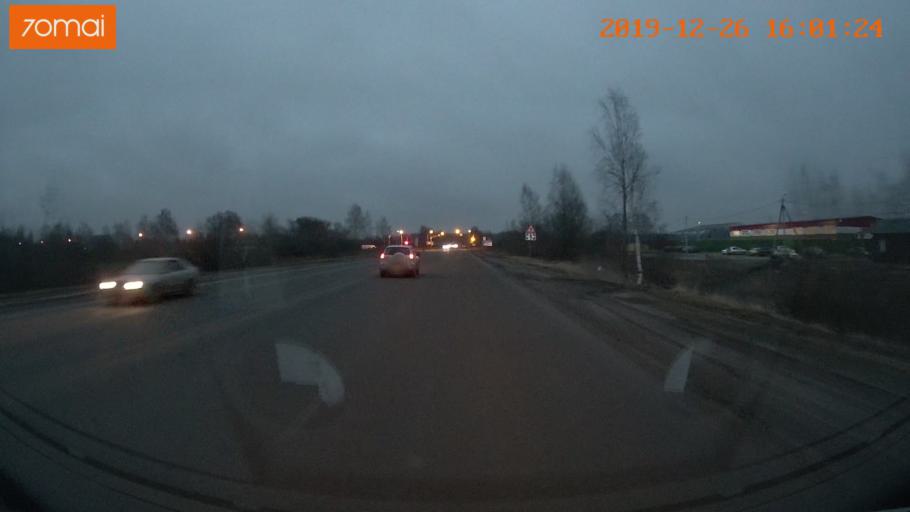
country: RU
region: Jaroslavl
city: Rybinsk
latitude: 58.0161
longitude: 38.8197
